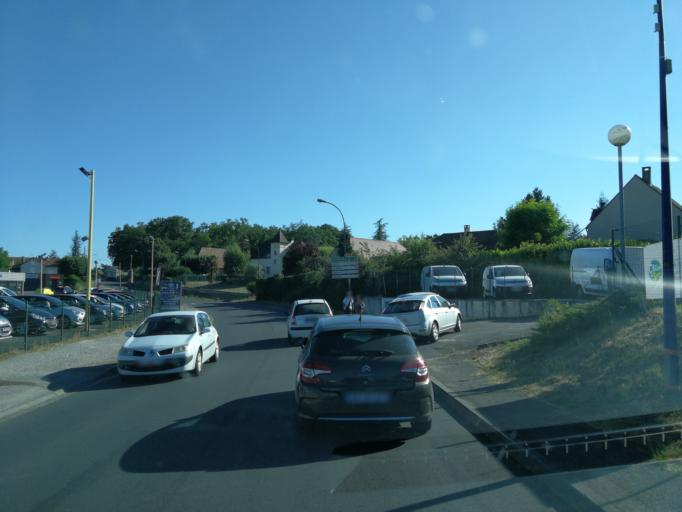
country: FR
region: Midi-Pyrenees
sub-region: Departement du Lot
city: Gourdon
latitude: 44.7311
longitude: 1.3742
